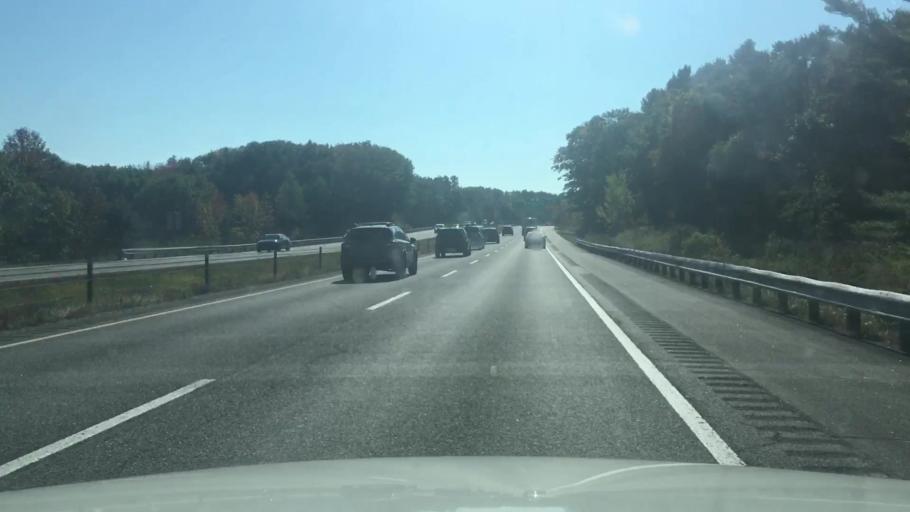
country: US
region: Maine
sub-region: Cumberland County
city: Falmouth
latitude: 43.7364
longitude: -70.2281
